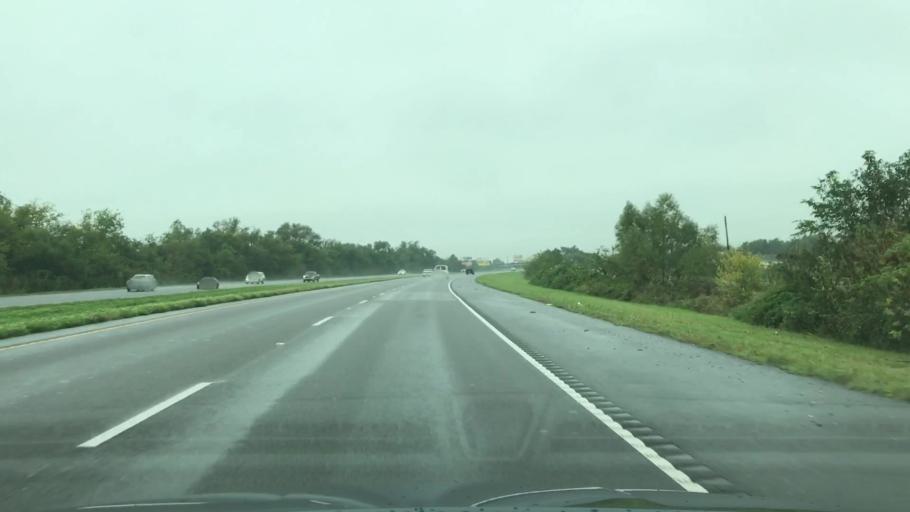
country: US
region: Louisiana
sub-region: Lafourche Parish
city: Raceland
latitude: 29.6909
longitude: -90.5925
